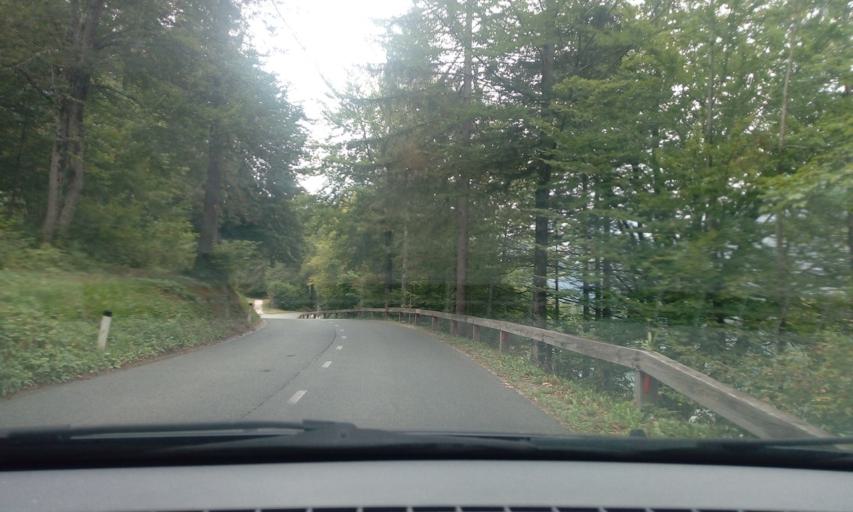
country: SI
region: Bohinj
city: Bohinjska Bistrica
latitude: 46.2789
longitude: 13.8658
